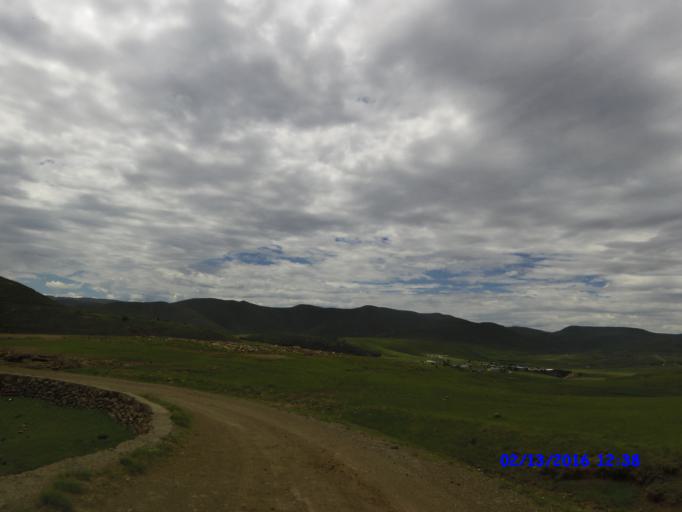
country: LS
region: Maseru
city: Nako
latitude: -29.8369
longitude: 28.0280
